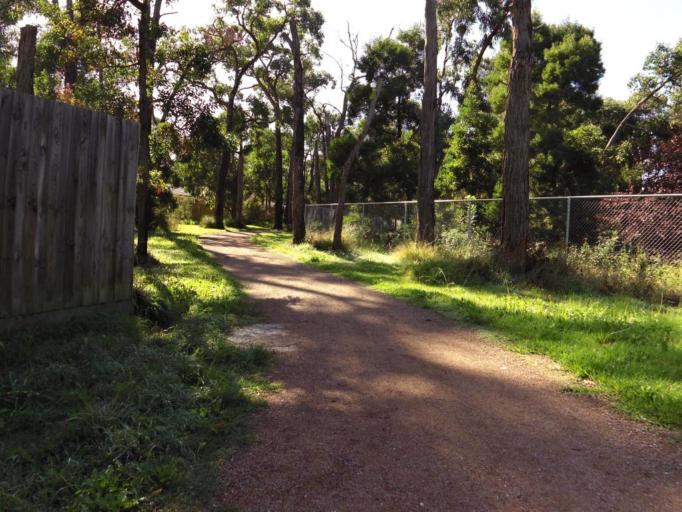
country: AU
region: Victoria
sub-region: Yarra Ranges
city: Kilsyth
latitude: -37.8049
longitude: 145.2968
